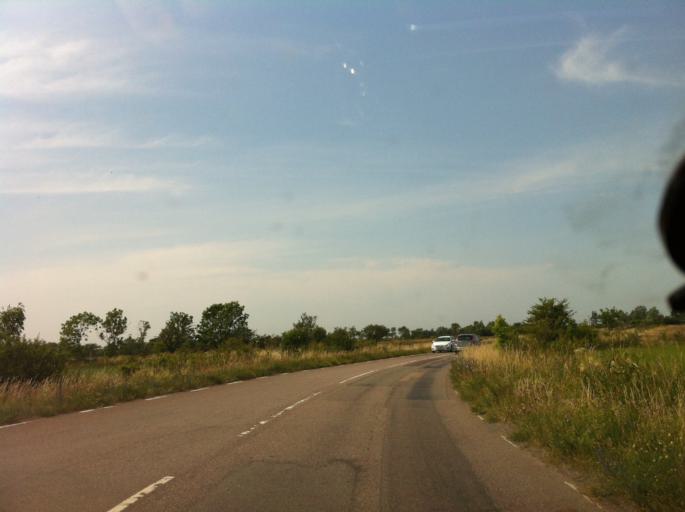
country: SE
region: Kalmar
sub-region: Borgholms Kommun
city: Borgholm
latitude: 57.0584
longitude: 16.8785
